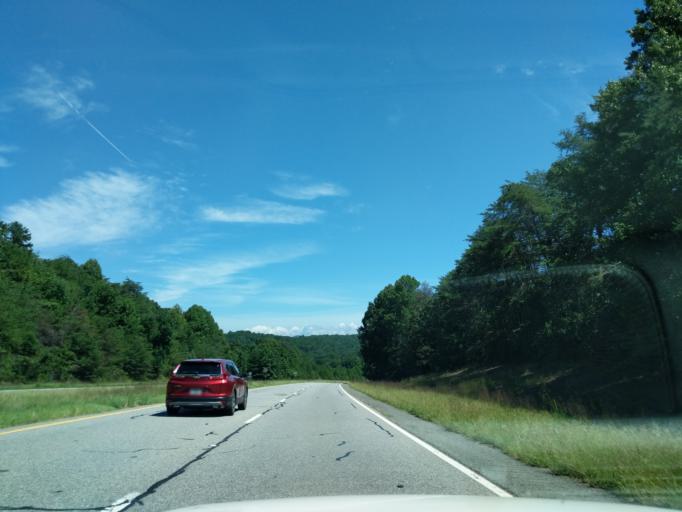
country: US
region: Georgia
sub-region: Fannin County
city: Blue Ridge
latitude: 34.8936
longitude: -84.2566
